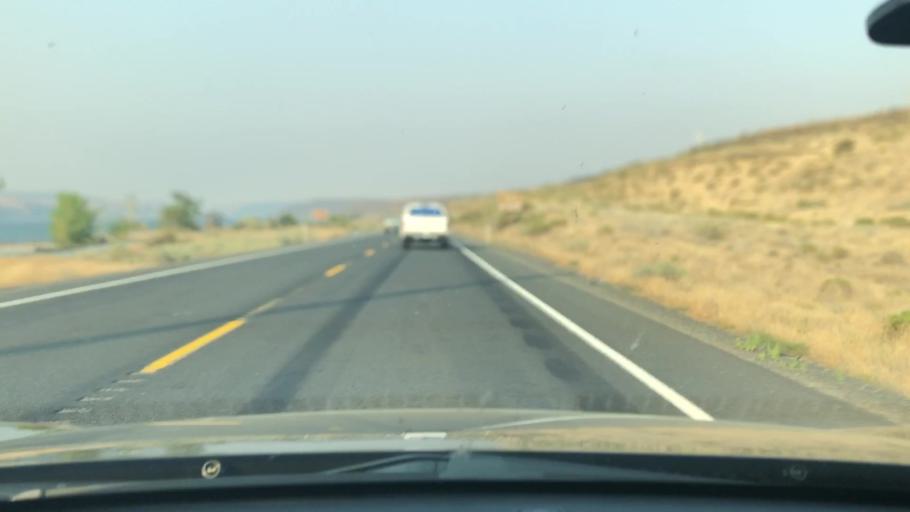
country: US
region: Oregon
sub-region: Umatilla County
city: Stanfield
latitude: 45.9213
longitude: -119.1201
